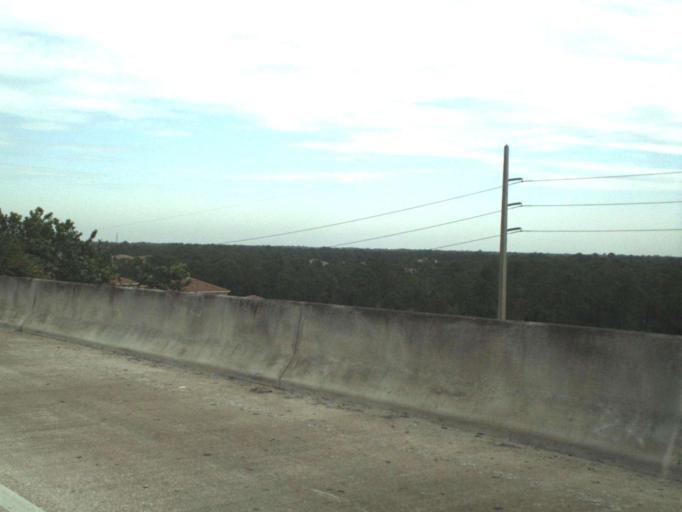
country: US
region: Florida
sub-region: Martin County
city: Palm City
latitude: 27.1208
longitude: -80.2709
